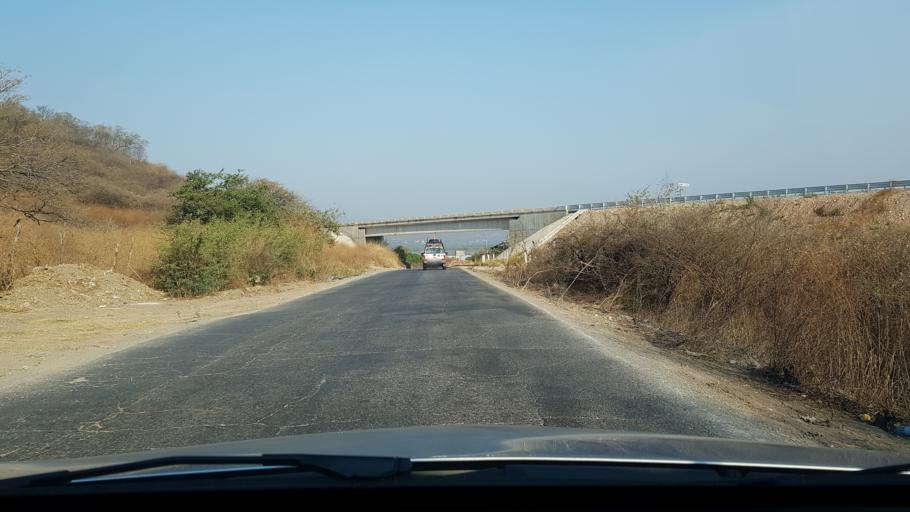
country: MX
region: Morelos
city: Tlaltizapan
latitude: 18.6779
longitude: -99.0798
